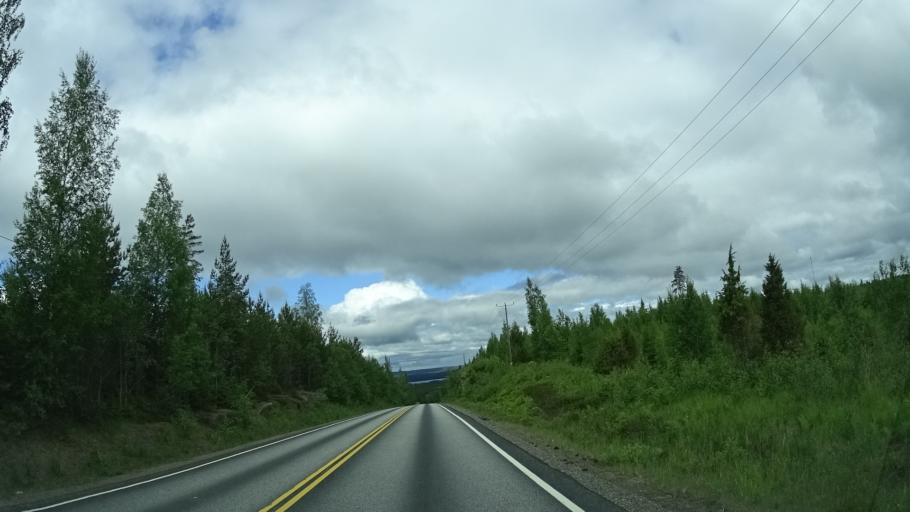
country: FI
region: Central Finland
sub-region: Joutsa
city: Luhanka
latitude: 61.9394
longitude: 25.7127
